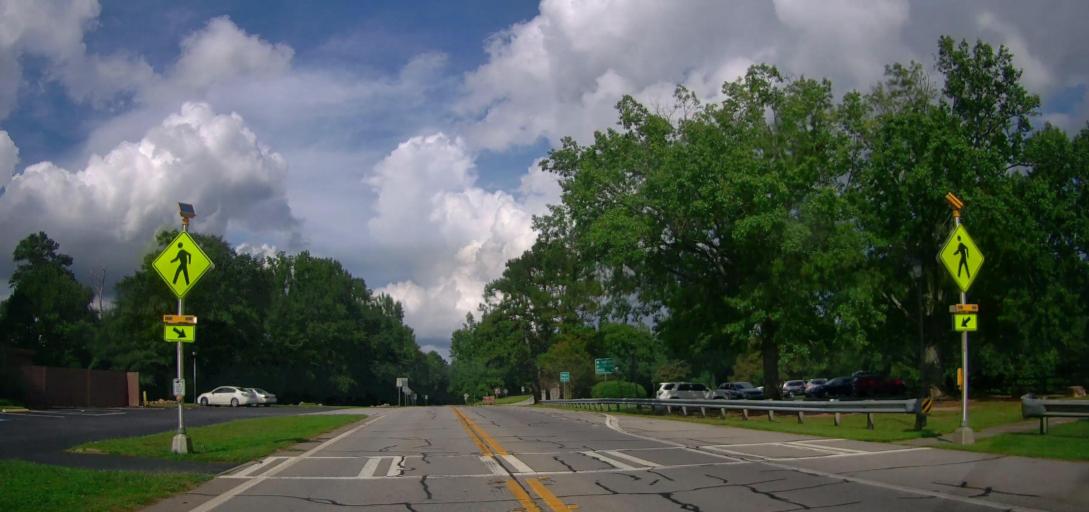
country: US
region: Georgia
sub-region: Harris County
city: Pine Mountain
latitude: 32.8105
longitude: -84.8562
